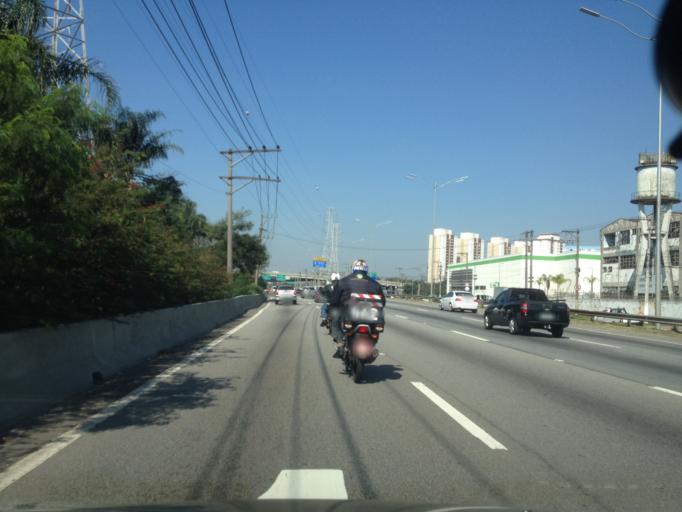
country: BR
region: Sao Paulo
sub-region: Osasco
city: Osasco
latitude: -23.5439
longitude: -46.7376
